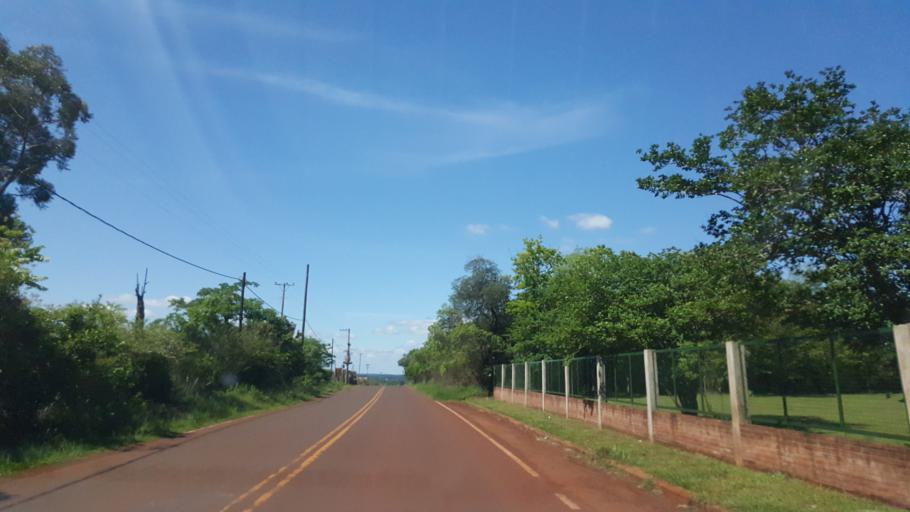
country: AR
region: Misiones
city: Garupa
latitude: -27.5012
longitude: -55.8484
